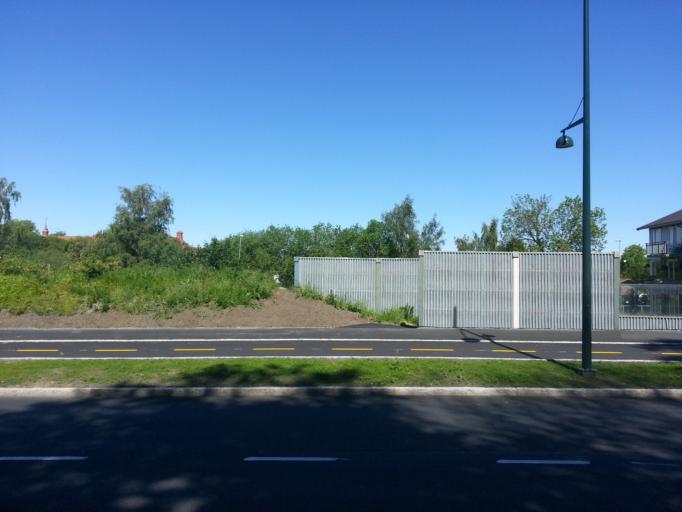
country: NO
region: Sor-Trondelag
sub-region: Trondheim
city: Trondheim
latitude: 63.4372
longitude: 10.4501
